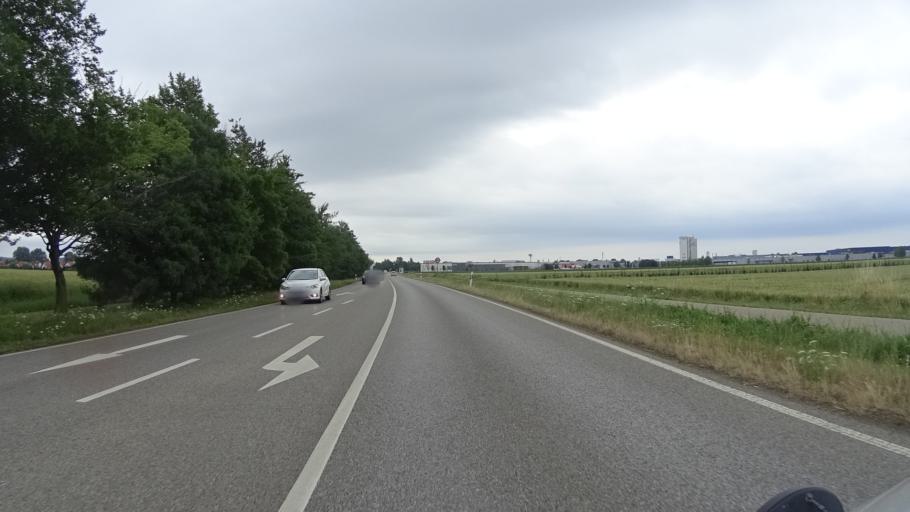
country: DE
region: Bavaria
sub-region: Swabia
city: Heimertingen
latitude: 48.0100
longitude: 10.1668
